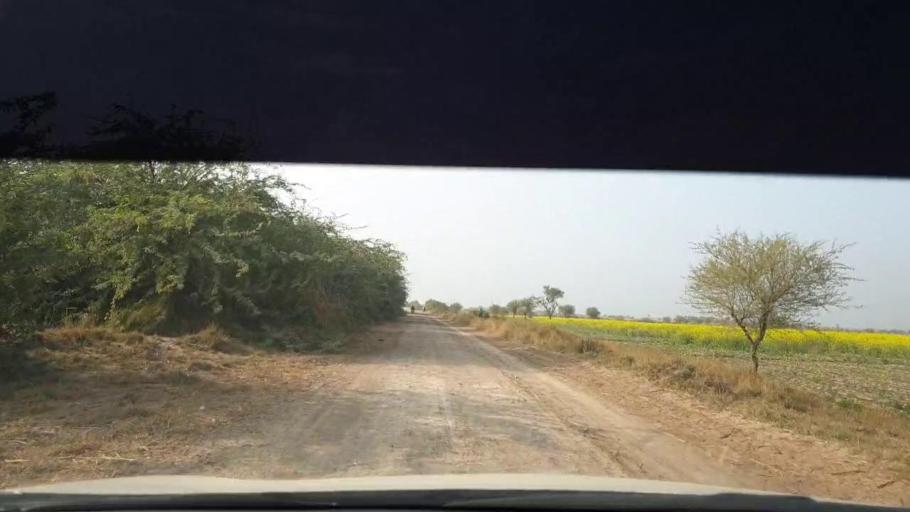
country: PK
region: Sindh
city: Berani
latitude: 25.7498
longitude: 68.9430
